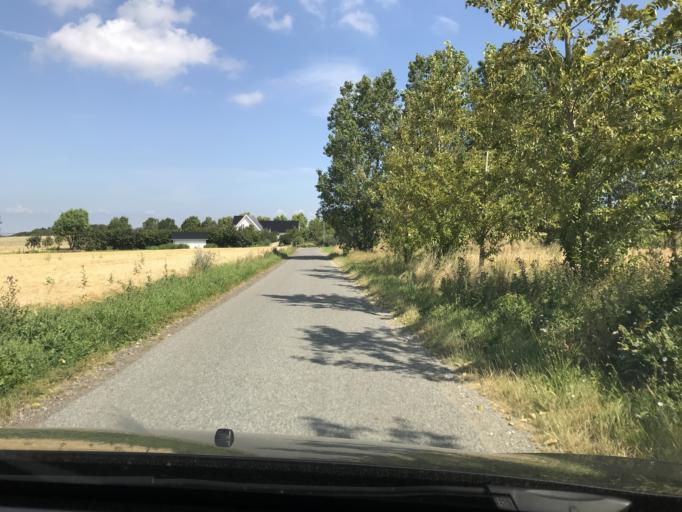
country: DK
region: South Denmark
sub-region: AEro Kommune
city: AEroskobing
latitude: 54.8876
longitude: 10.3941
